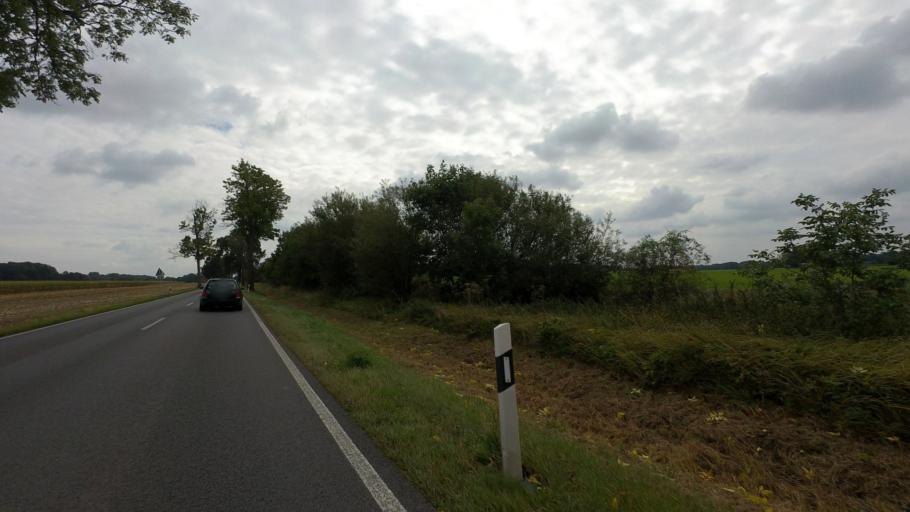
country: DE
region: Brandenburg
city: Golssen
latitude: 51.9589
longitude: 13.6283
